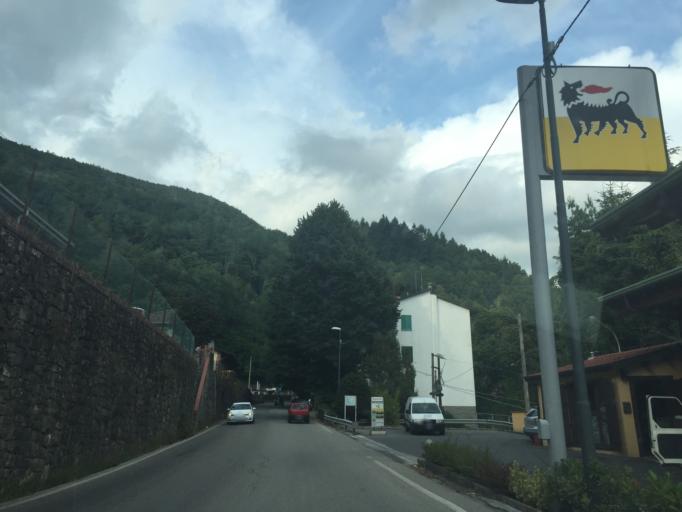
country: IT
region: Tuscany
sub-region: Provincia di Pistoia
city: San Marcello Pistoiese
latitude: 44.0566
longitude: 10.7793
